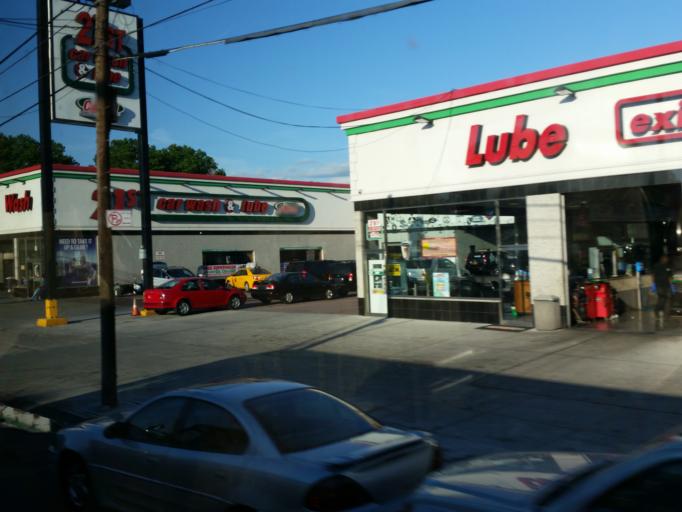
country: US
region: New York
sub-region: Queens County
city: Long Island City
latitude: 40.7590
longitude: -73.9376
